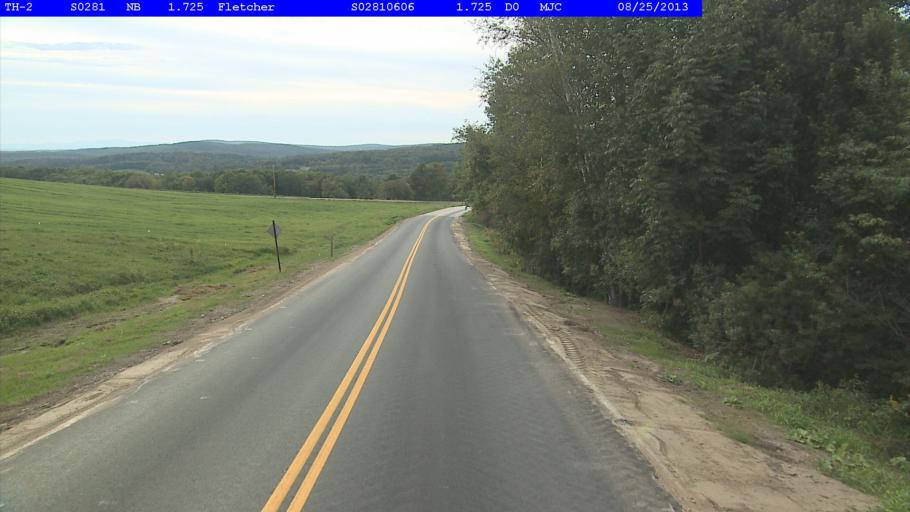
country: US
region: Vermont
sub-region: Franklin County
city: Saint Albans
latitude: 44.6999
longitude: -72.9359
